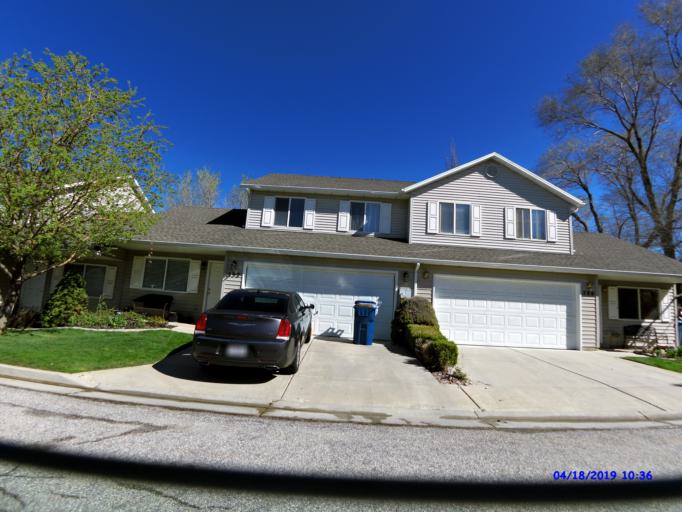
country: US
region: Utah
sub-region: Weber County
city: Harrisville
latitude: 41.2726
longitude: -111.9645
